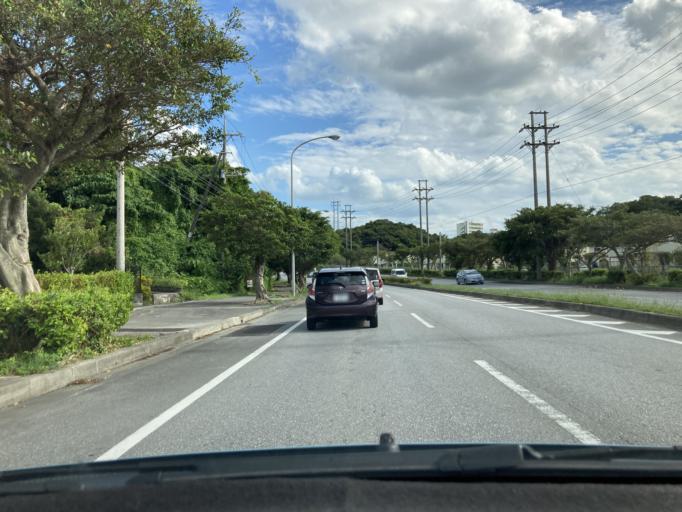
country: JP
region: Okinawa
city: Okinawa
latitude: 26.3575
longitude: 127.8018
